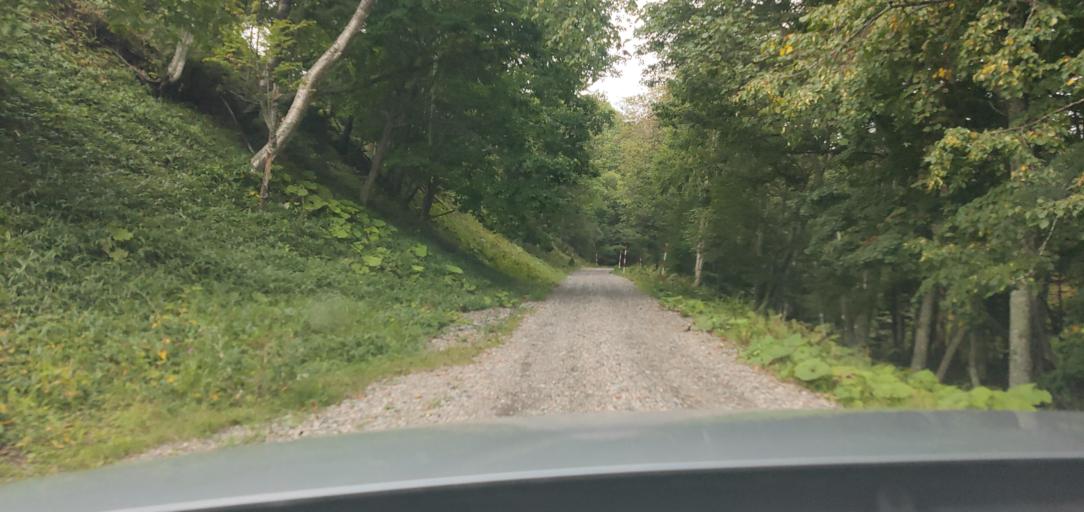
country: JP
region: Hokkaido
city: Kitami
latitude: 43.3662
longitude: 143.9333
